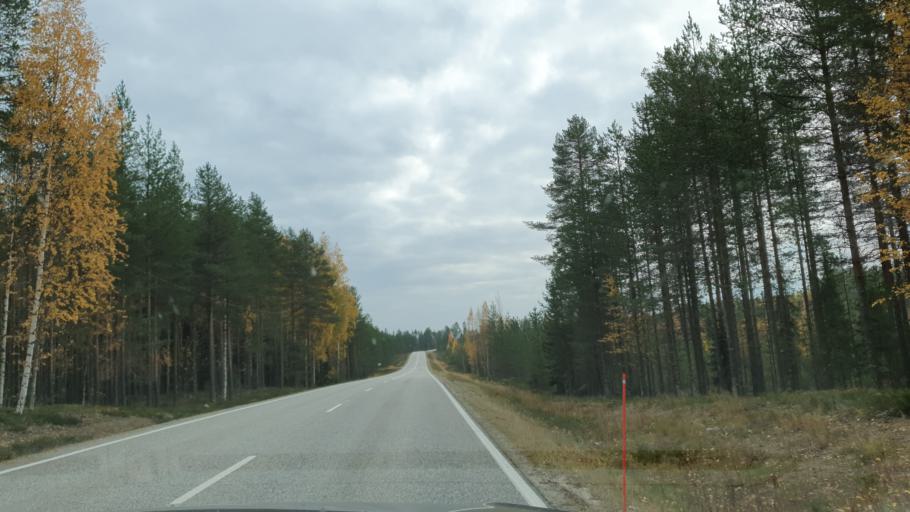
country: FI
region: Kainuu
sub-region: Kehys-Kainuu
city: Puolanka
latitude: 65.2369
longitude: 27.5894
